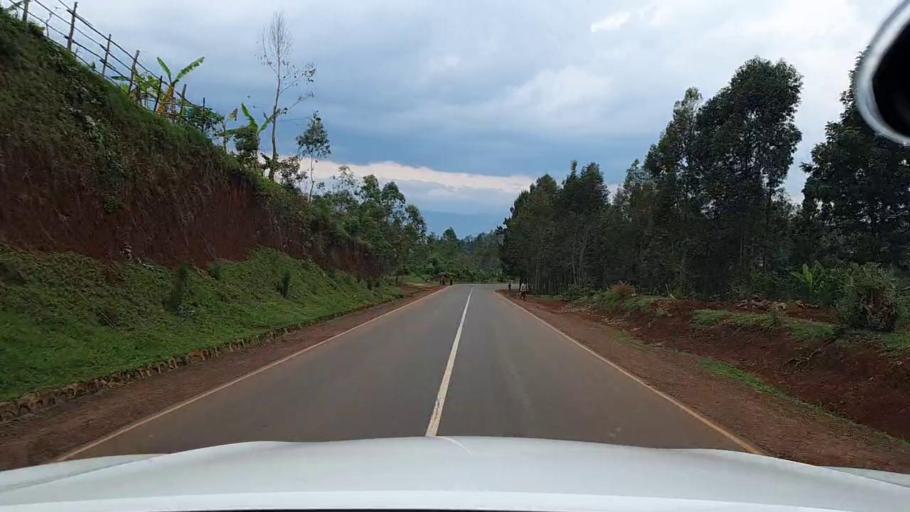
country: RW
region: Western Province
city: Cyangugu
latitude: -2.6450
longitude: 28.9552
